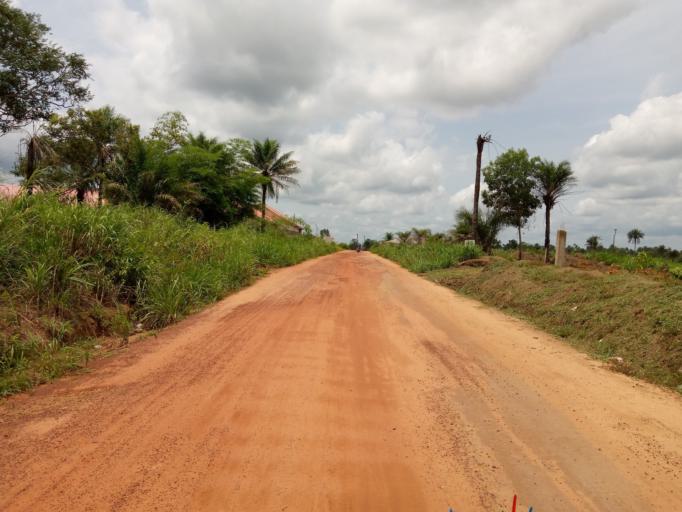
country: SL
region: Western Area
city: Waterloo
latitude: 8.3528
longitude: -12.9587
